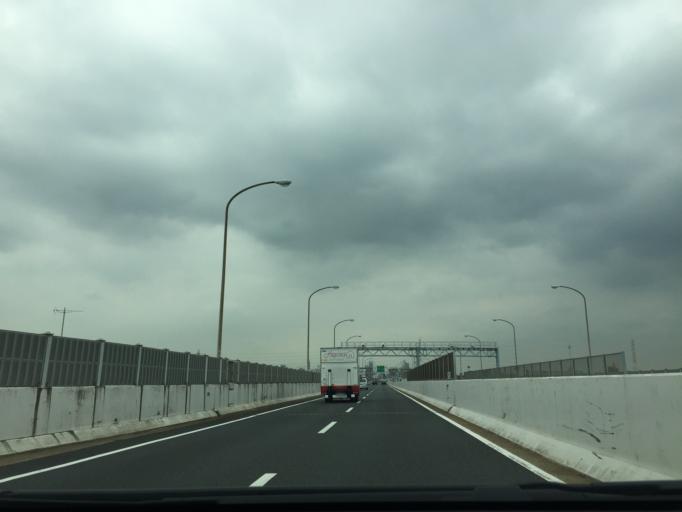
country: JP
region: Aichi
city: Obu
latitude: 35.0883
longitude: 136.9324
